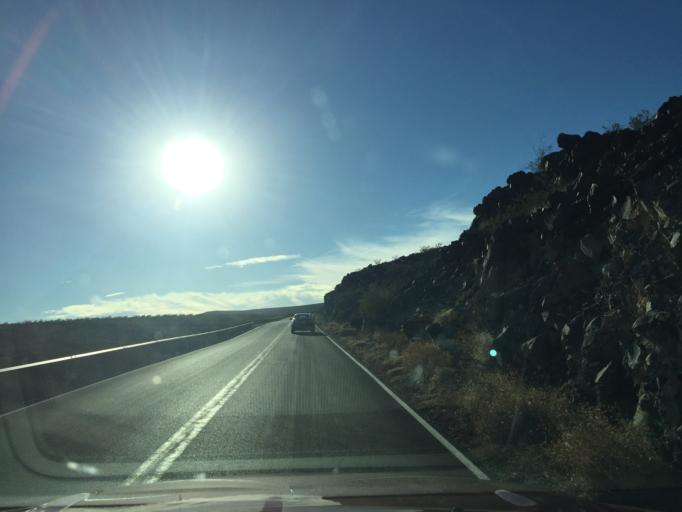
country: US
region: California
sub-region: Inyo County
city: Lone Pine
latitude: 36.3491
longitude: -117.5466
